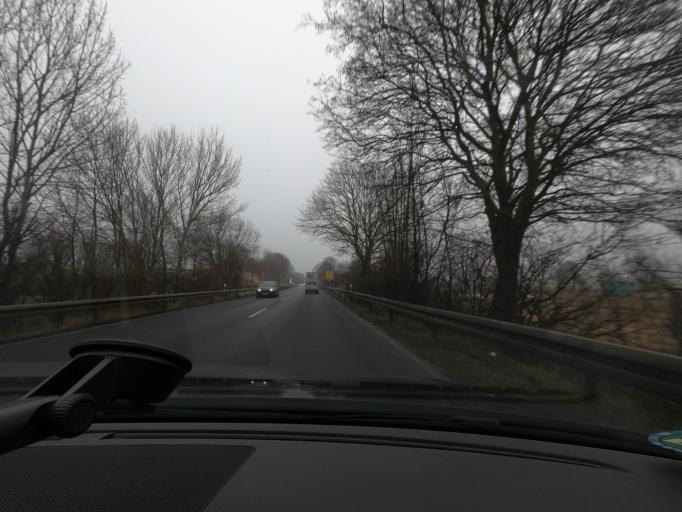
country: DE
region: North Rhine-Westphalia
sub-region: Regierungsbezirk Koln
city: Merzenich
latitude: 50.8183
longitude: 6.5299
